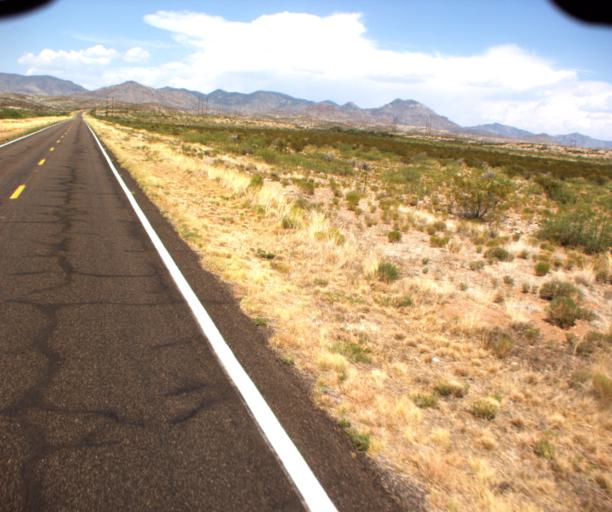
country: US
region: Arizona
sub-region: Greenlee County
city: Clifton
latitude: 32.9765
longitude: -109.1943
